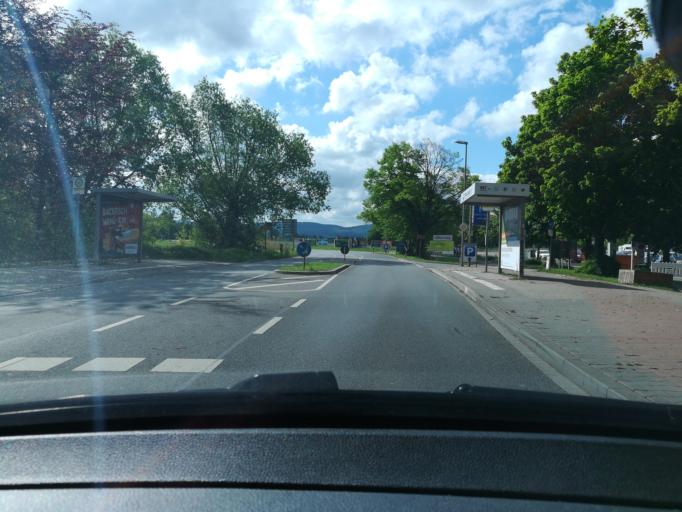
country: DE
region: North Rhine-Westphalia
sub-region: Regierungsbezirk Detmold
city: Minden
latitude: 52.2880
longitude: 8.9264
